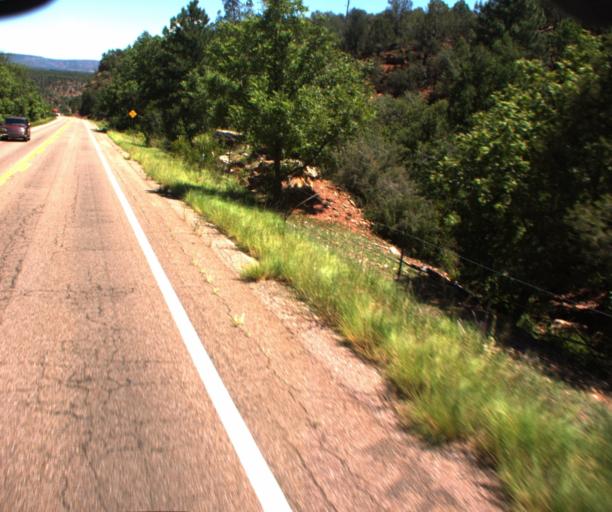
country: US
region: Arizona
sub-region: Navajo County
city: Cibecue
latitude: 33.9770
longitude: -110.3121
